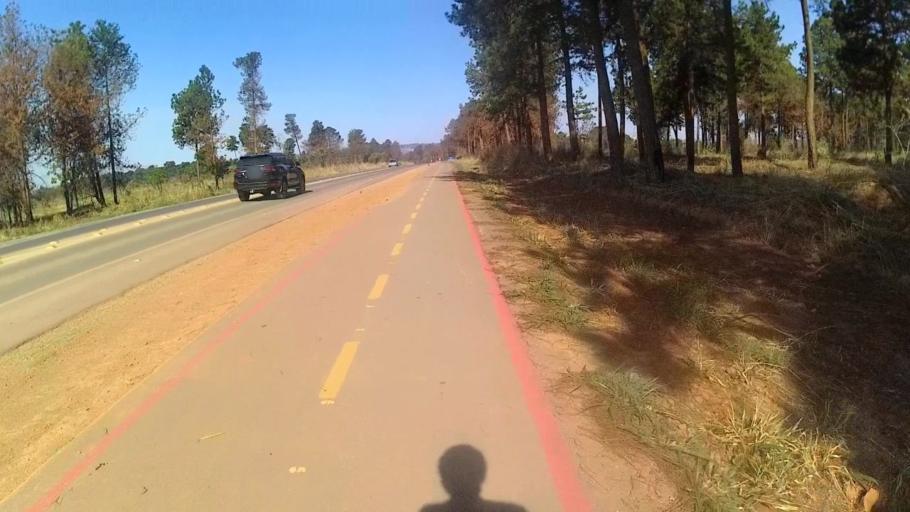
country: BR
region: Federal District
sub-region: Brasilia
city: Brasilia
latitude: -15.6792
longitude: -48.2154
